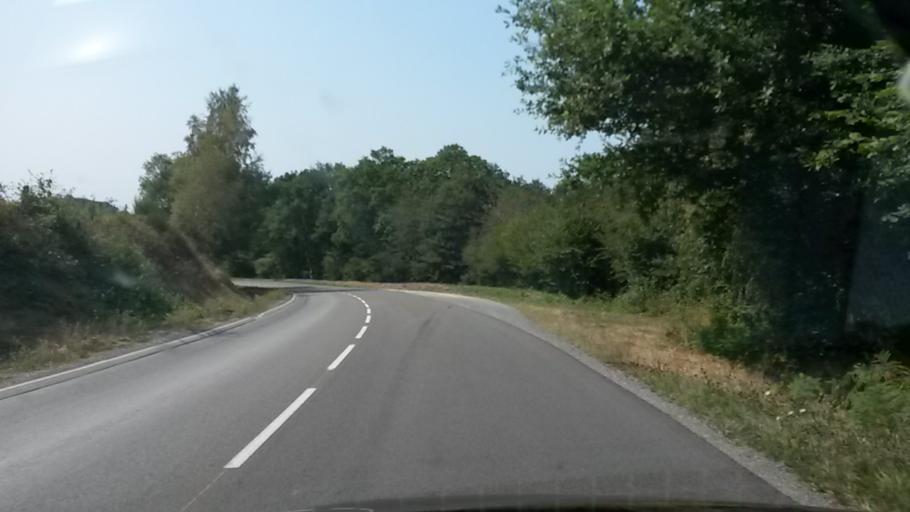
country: FR
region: Pays de la Loire
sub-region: Departement de la Mayenne
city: Villaines-la-Juhel
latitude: 48.3593
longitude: -0.2314
